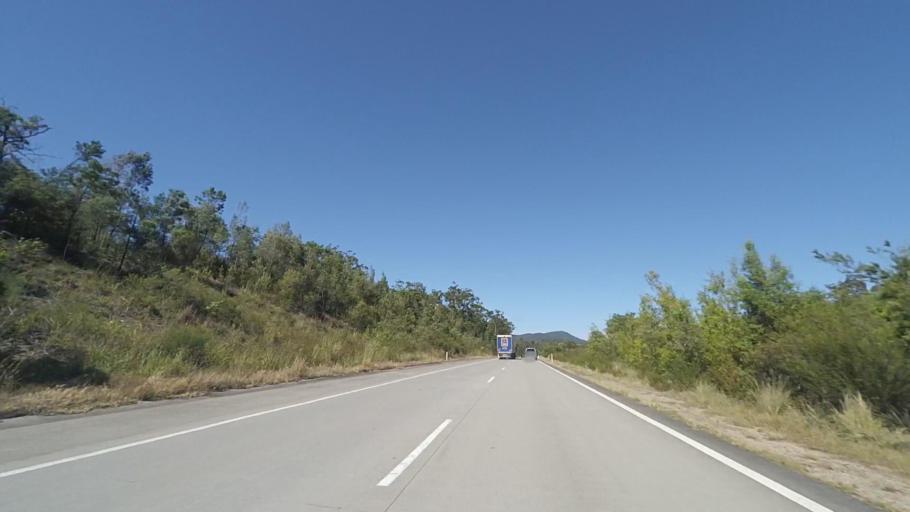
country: AU
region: New South Wales
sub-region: Port Stephens Shire
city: Port Stephens
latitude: -32.6208
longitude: 152.0684
